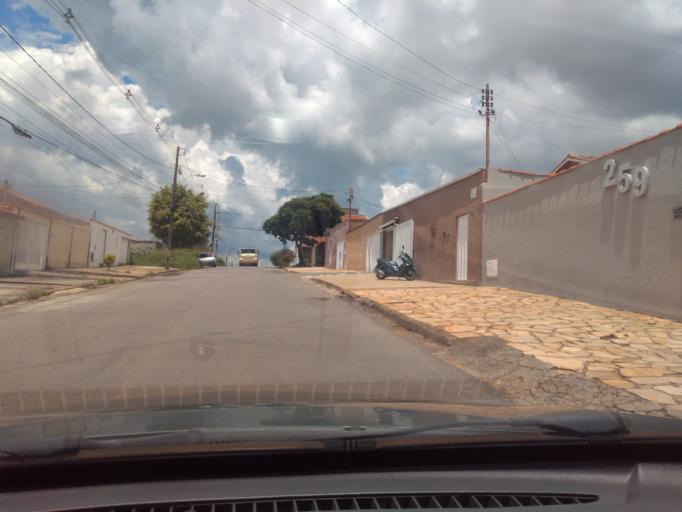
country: BR
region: Minas Gerais
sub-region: Tres Coracoes
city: Tres Coracoes
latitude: -21.6787
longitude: -45.2711
